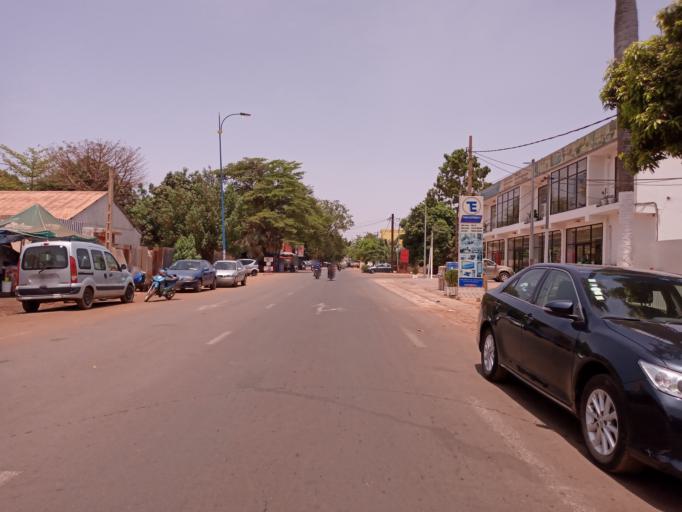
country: ML
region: Bamako
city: Bamako
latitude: 12.6336
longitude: -7.9998
